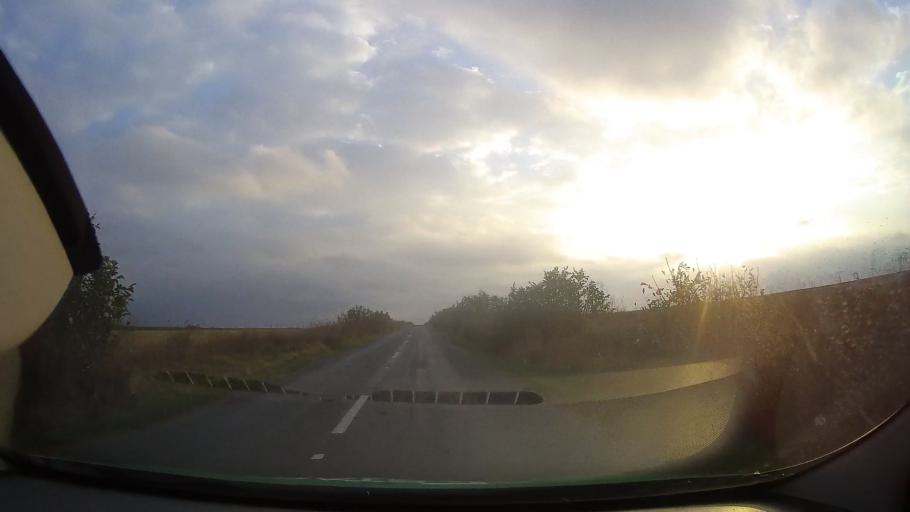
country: RO
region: Constanta
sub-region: Comuna Adamclisi
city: Adamclisi
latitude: 44.0246
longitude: 27.9085
